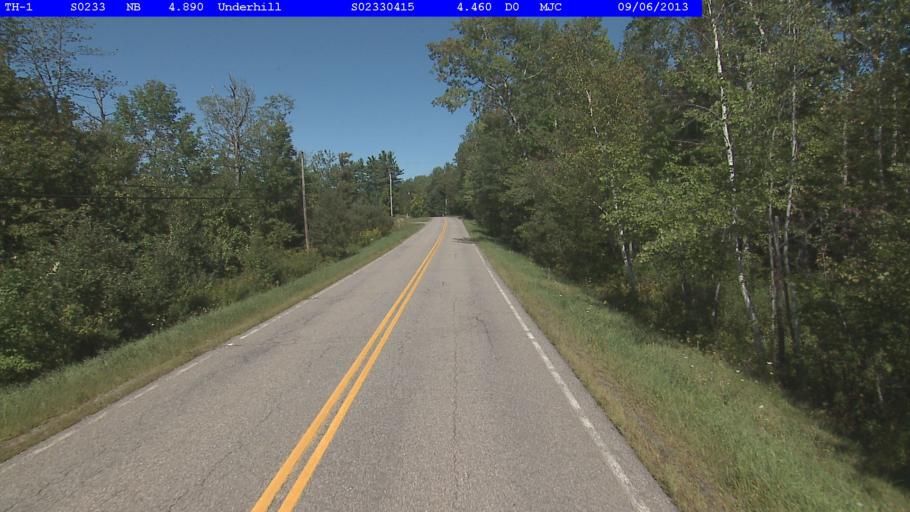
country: US
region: Vermont
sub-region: Chittenden County
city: Jericho
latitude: 44.5305
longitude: -72.8757
